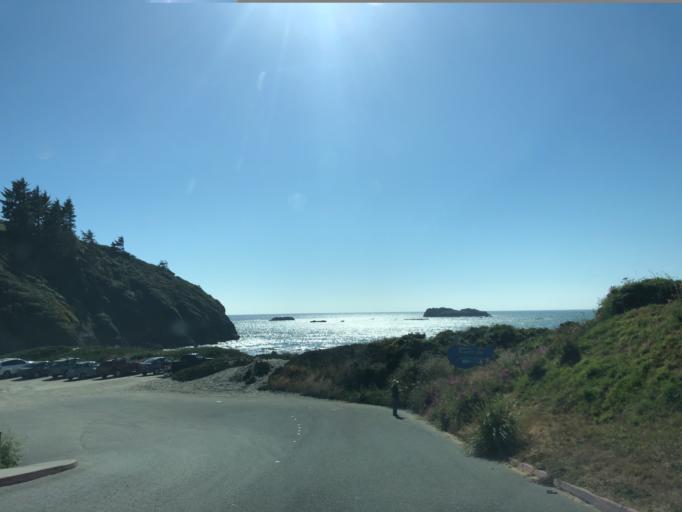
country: US
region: California
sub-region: Humboldt County
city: Westhaven-Moonstone
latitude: 41.0577
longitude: -124.1486
